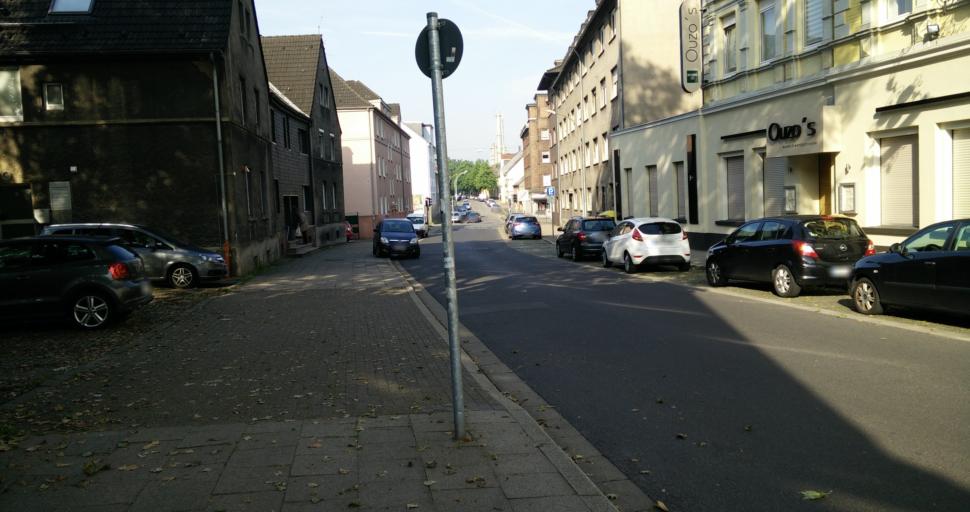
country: DE
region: North Rhine-Westphalia
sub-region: Regierungsbezirk Arnsberg
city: Herne
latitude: 51.5355
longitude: 7.2206
